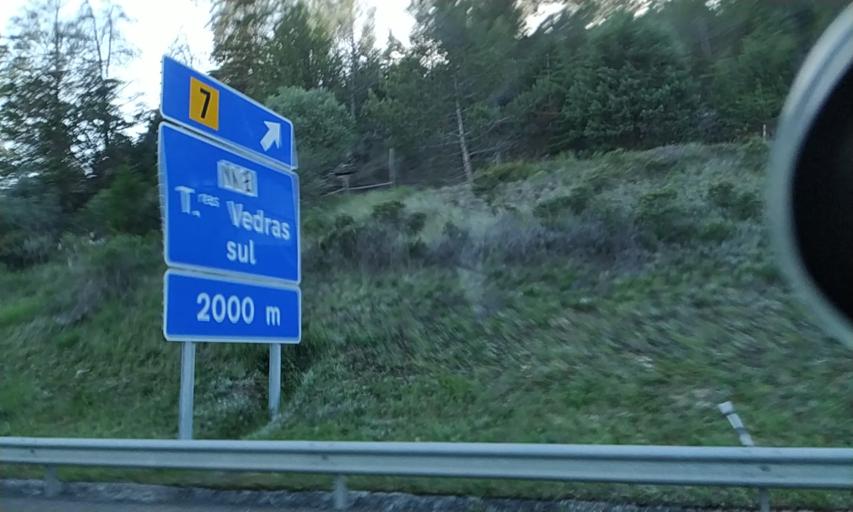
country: PT
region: Lisbon
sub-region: Torres Vedras
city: Torres Vedras
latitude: 39.0843
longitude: -9.2316
